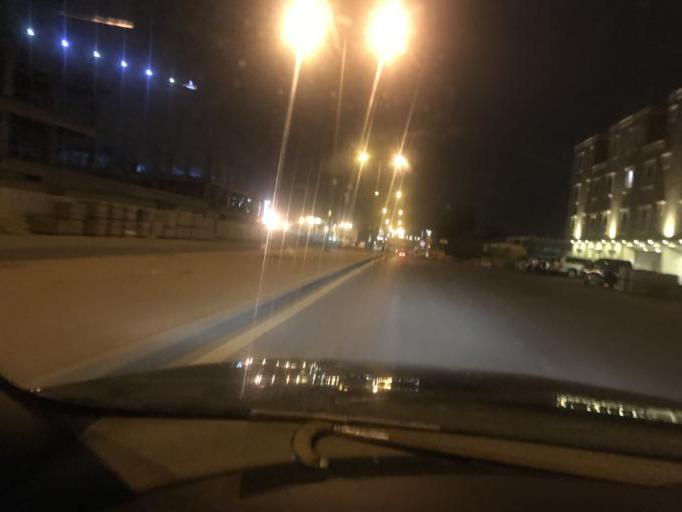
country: SA
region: Ar Riyad
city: Riyadh
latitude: 24.7988
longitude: 46.6854
